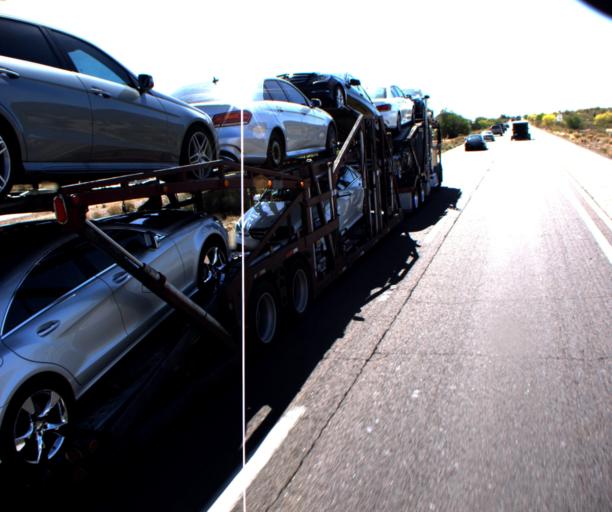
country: US
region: Arizona
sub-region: Pinal County
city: Sacaton
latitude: 33.0354
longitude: -111.7787
